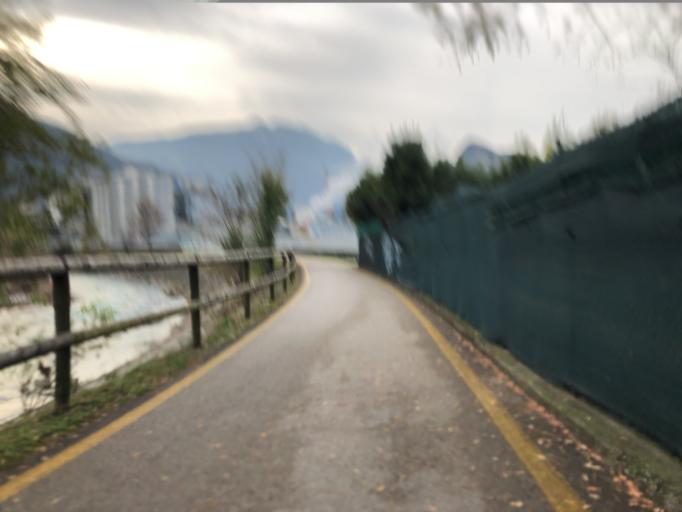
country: IT
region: Trentino-Alto Adige
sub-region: Provincia di Trento
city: Arco
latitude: 45.9069
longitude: 10.8799
